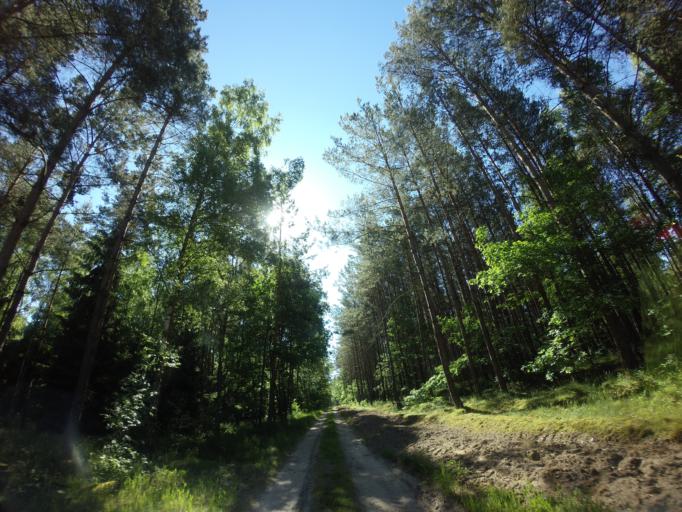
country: PL
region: West Pomeranian Voivodeship
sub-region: Powiat choszczenski
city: Drawno
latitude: 53.2332
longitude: 15.6918
